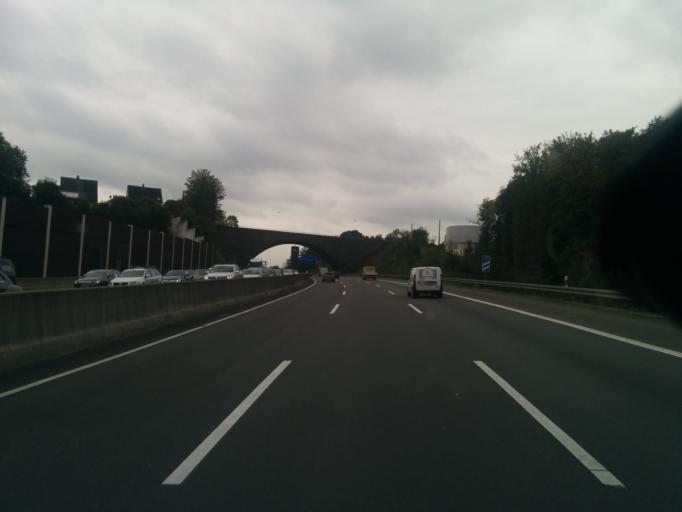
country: DE
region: North Rhine-Westphalia
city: Wermelskirchen
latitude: 51.1396
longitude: 7.1921
